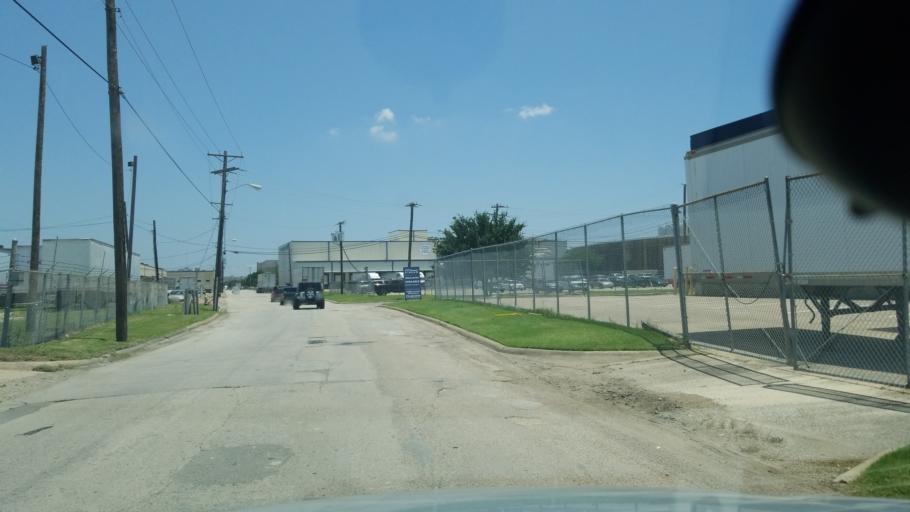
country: US
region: Texas
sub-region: Dallas County
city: Irving
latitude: 32.8122
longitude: -96.8786
